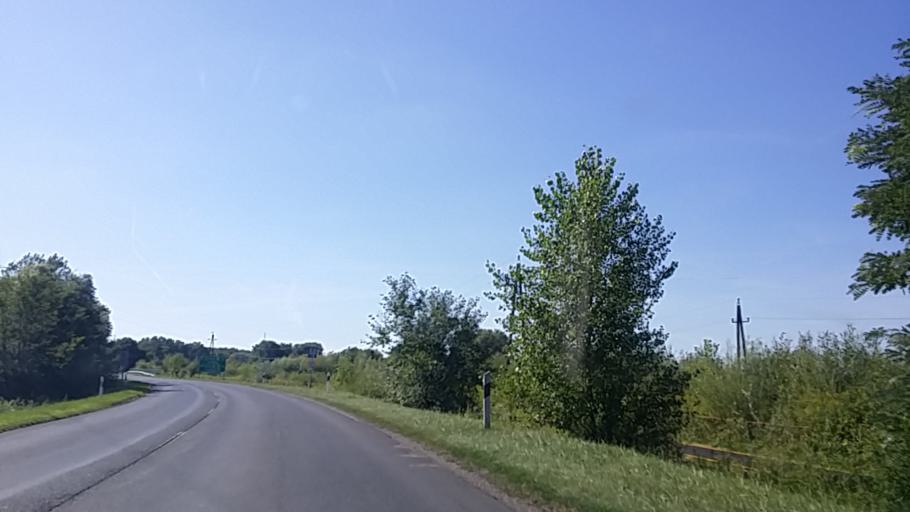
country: HU
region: Somogy
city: Balatonbereny
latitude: 46.7017
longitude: 17.2614
